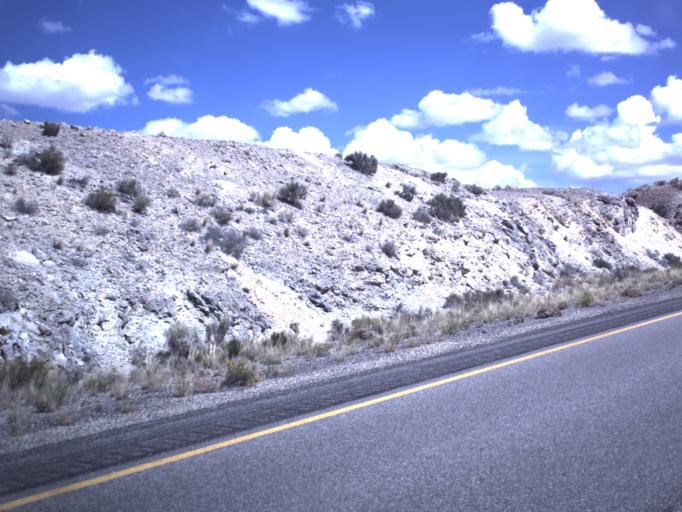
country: US
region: Utah
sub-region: Emery County
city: Ferron
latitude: 38.8454
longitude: -110.9899
